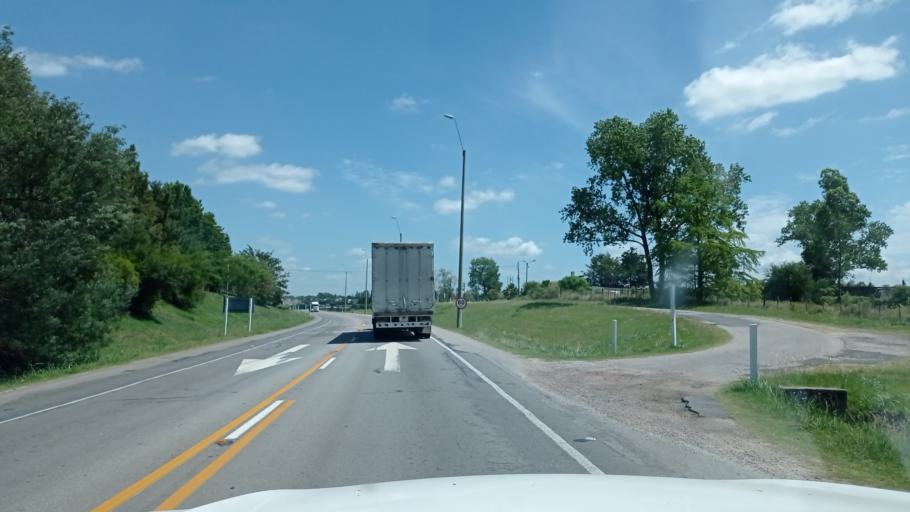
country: UY
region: Florida
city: Florida
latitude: -34.0948
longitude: -56.1979
